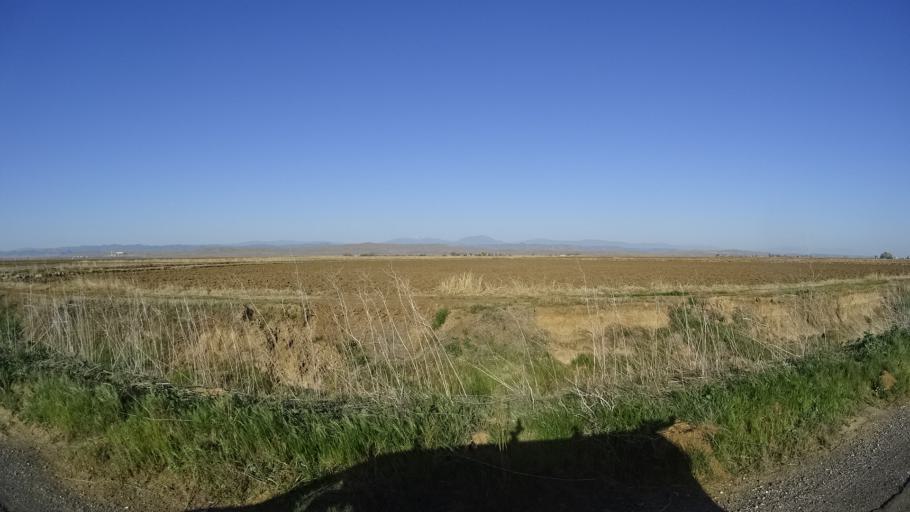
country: US
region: California
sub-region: Colusa County
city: Maxwell
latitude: 39.3944
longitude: -122.2300
